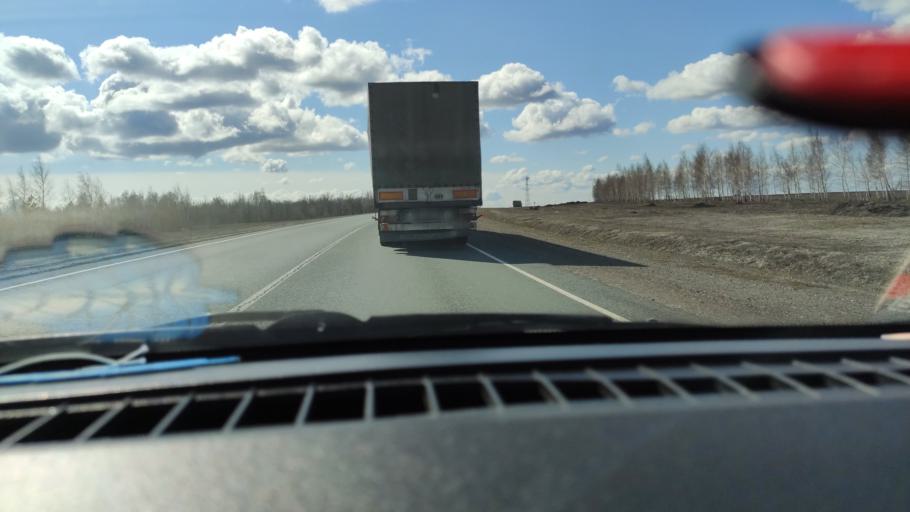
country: RU
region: Samara
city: Syzran'
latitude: 52.9320
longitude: 48.3071
